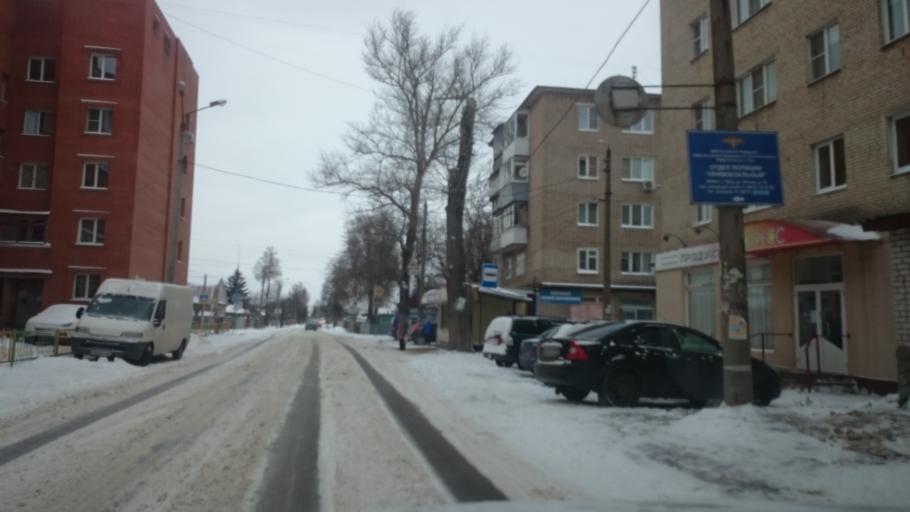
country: RU
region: Tula
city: Tula
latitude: 54.1979
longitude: 37.5613
